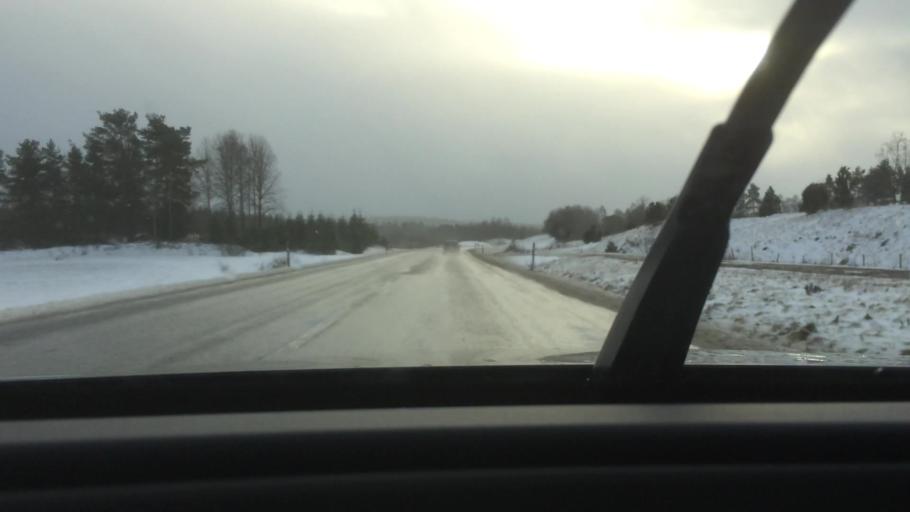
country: SE
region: Vaestra Goetaland
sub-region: Falkopings Kommun
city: Falkoeping
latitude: 57.9760
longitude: 13.5283
